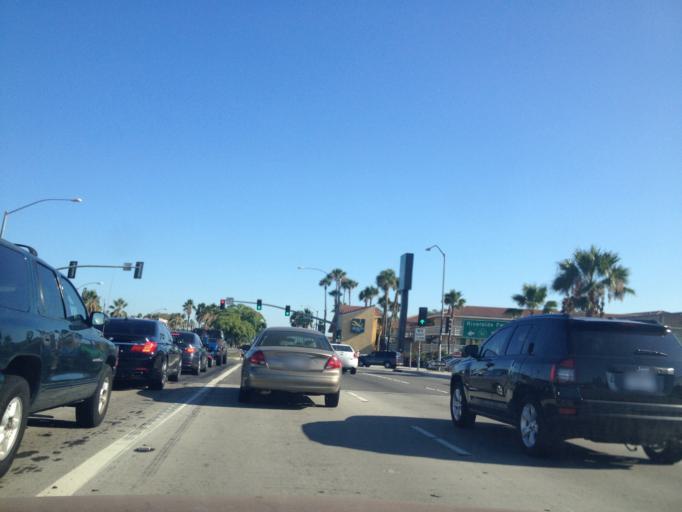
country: US
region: California
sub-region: Orange County
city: Fullerton
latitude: 33.8537
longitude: -117.9243
